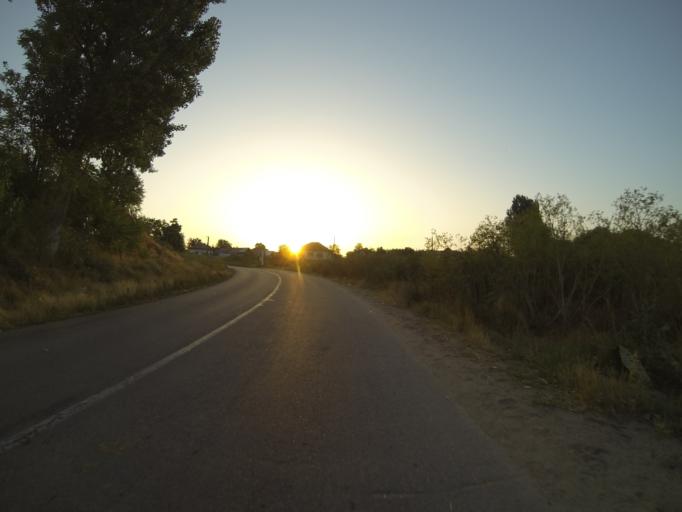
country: RO
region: Dolj
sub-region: Comuna Dobresti
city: Dobresti
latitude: 43.9828
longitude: 23.9387
